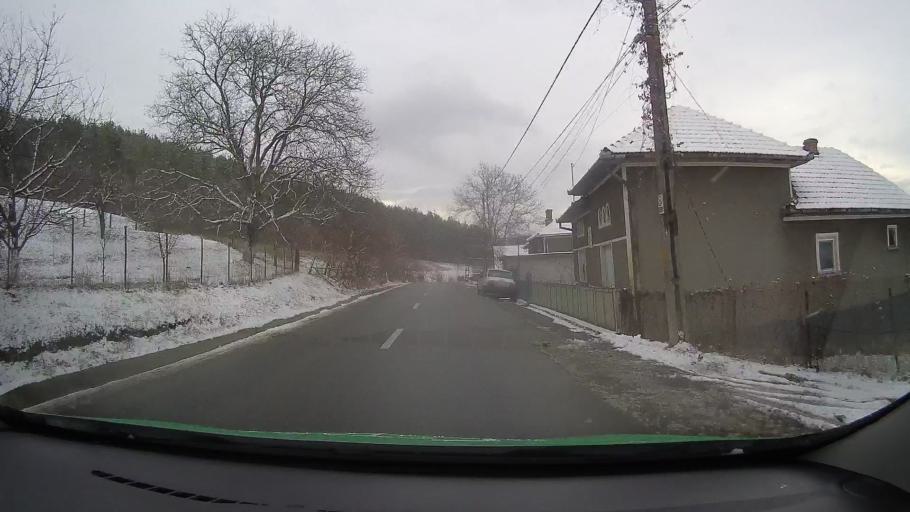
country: RO
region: Hunedoara
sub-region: Oras Hateg
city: Hateg
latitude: 45.6264
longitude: 22.9345
